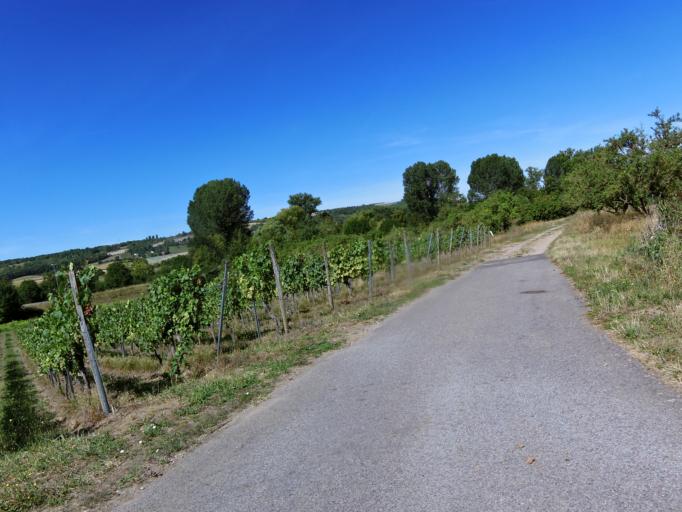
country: DE
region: Bavaria
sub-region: Regierungsbezirk Unterfranken
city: Randersacker
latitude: 49.7469
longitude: 9.9898
